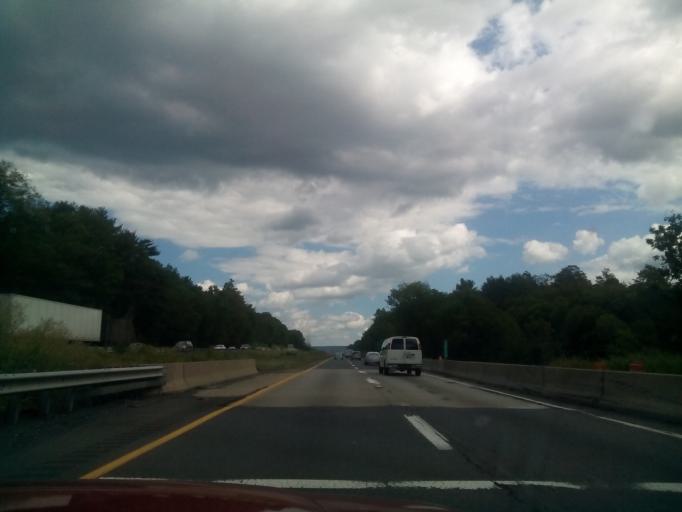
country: US
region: Pennsylvania
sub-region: Monroe County
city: Arlington Heights
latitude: 40.9933
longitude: -75.2560
